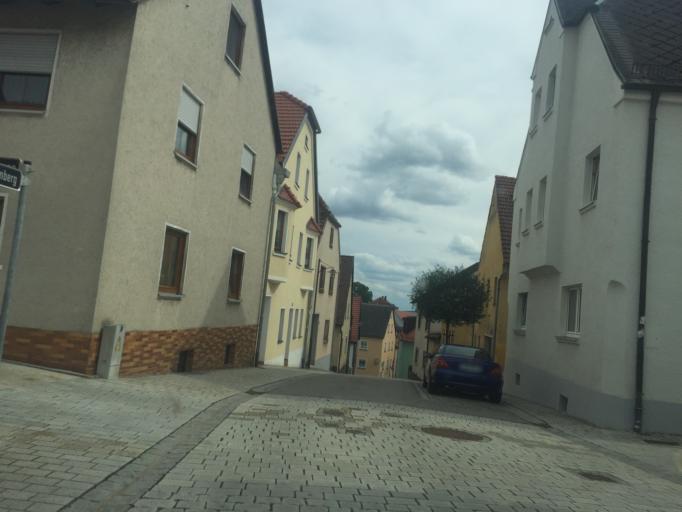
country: DE
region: Bavaria
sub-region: Upper Palatinate
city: Pressath
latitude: 49.7703
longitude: 11.9344
